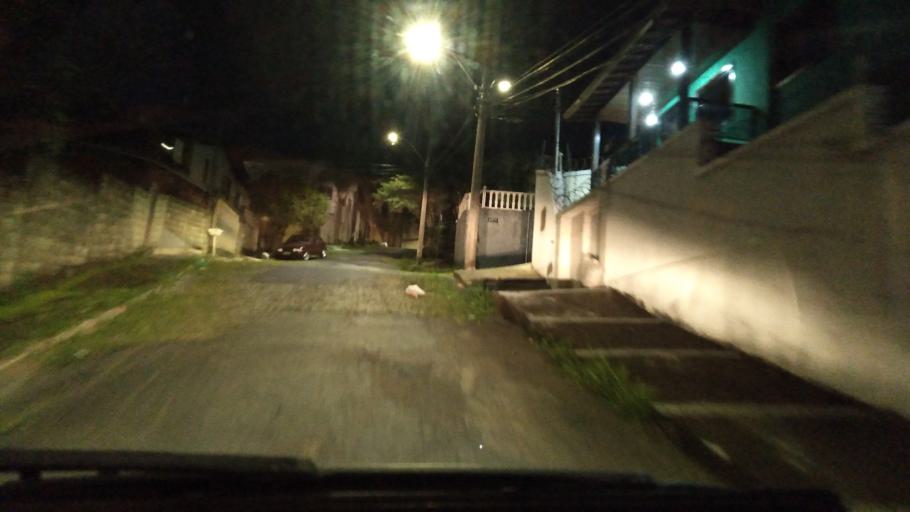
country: BR
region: Minas Gerais
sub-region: Belo Horizonte
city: Belo Horizonte
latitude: -19.8981
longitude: -43.9744
